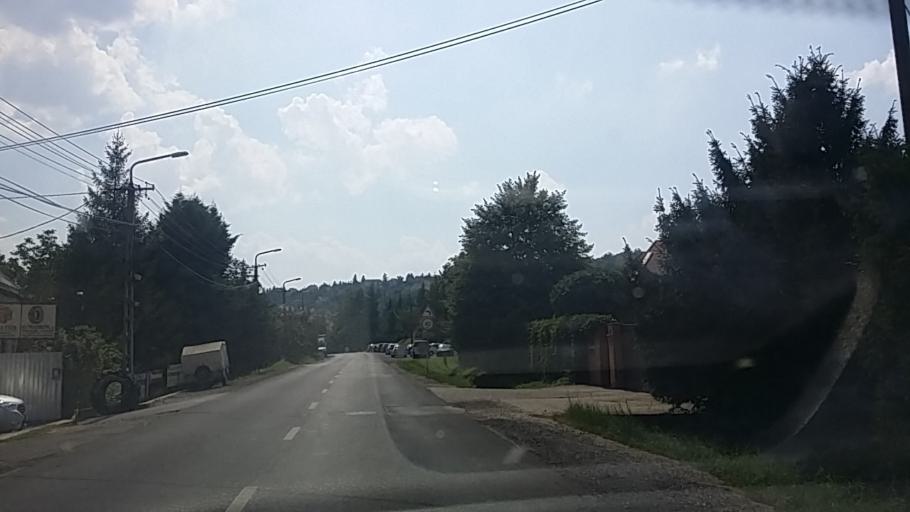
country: HU
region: Baranya
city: Pecs
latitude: 46.0780
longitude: 18.1887
